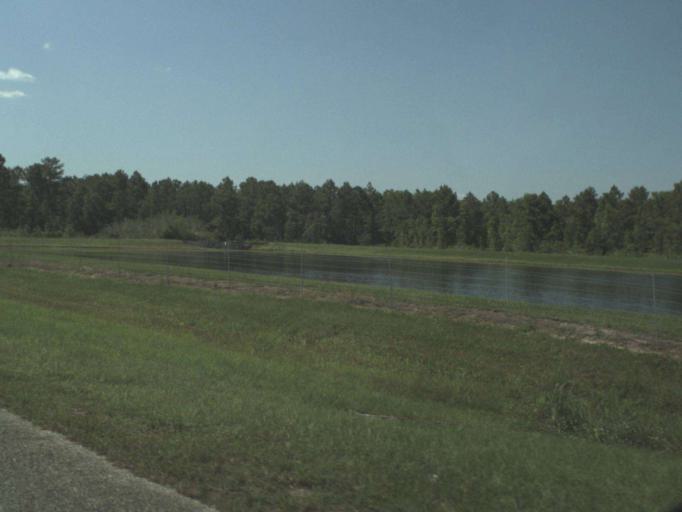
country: US
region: Florida
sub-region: Orange County
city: Wedgefield
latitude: 28.4878
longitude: -81.0369
